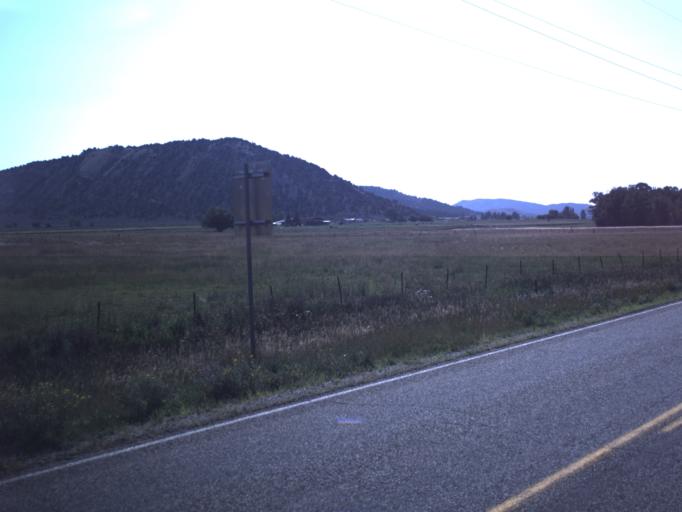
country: US
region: Utah
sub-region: Duchesne County
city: Duchesne
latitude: 40.3956
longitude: -110.7548
